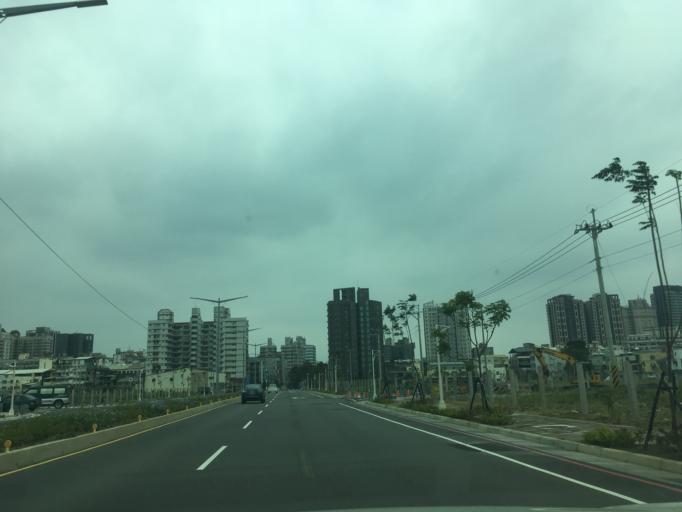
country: TW
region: Taiwan
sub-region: Taichung City
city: Taichung
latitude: 24.1802
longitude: 120.6768
